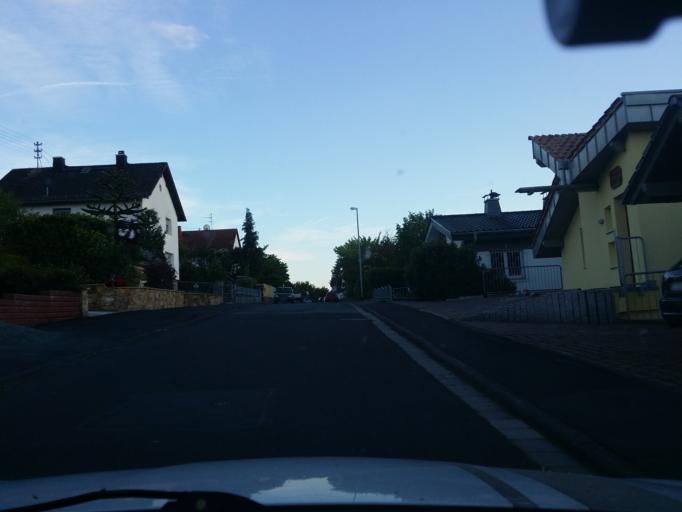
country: DE
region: Hesse
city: Bad Camberg
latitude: 50.2687
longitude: 8.2819
